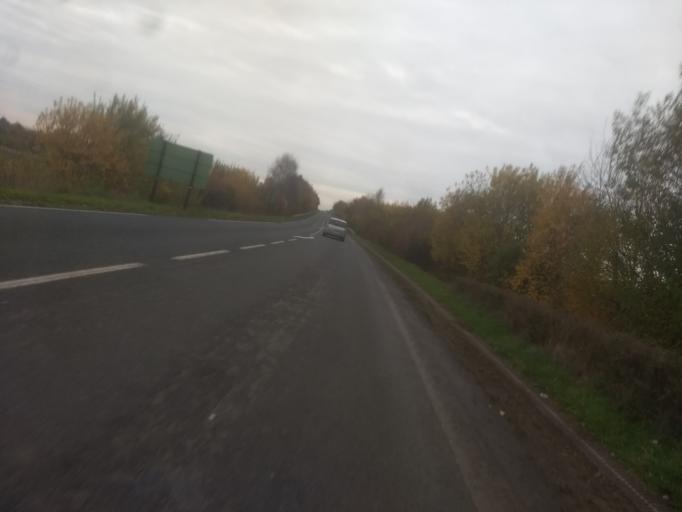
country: FR
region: Nord-Pas-de-Calais
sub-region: Departement du Pas-de-Calais
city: Achicourt
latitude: 50.2772
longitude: 2.7425
